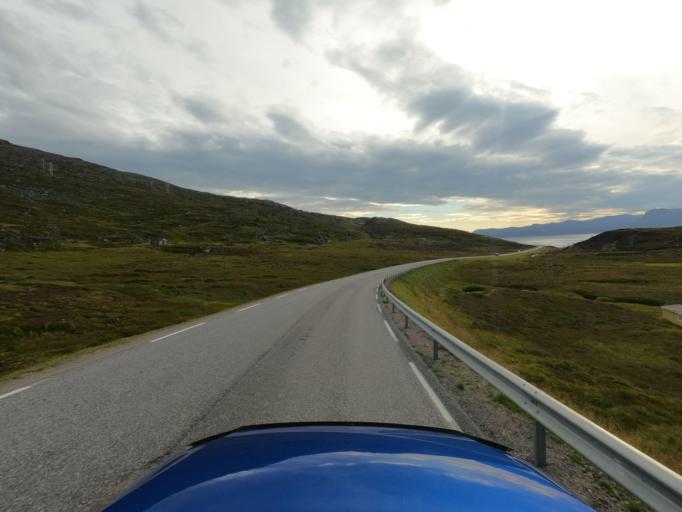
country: NO
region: Finnmark Fylke
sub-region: Hammerfest
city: Rypefjord
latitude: 70.6010
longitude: 23.6877
